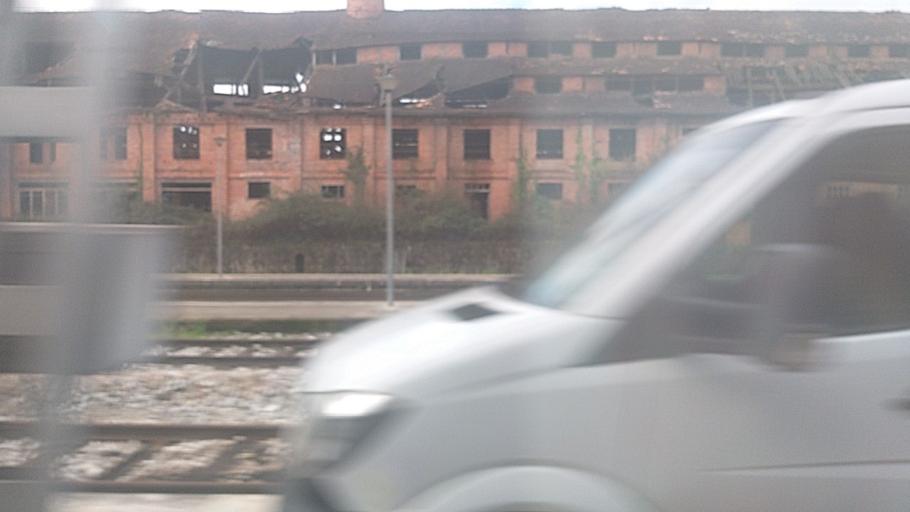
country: PT
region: Aveiro
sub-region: Mealhada
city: Pampilhosa do Botao
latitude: 40.3389
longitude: -8.4318
